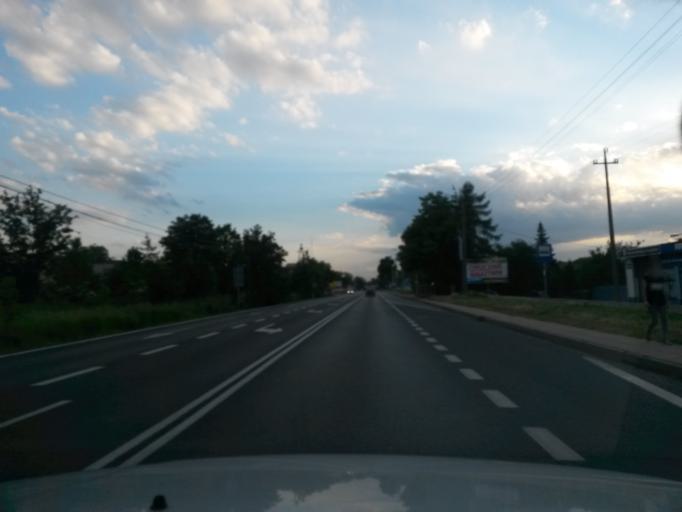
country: PL
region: Lodz Voivodeship
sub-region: Powiat wielunski
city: Wielun
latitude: 51.2263
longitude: 18.5892
